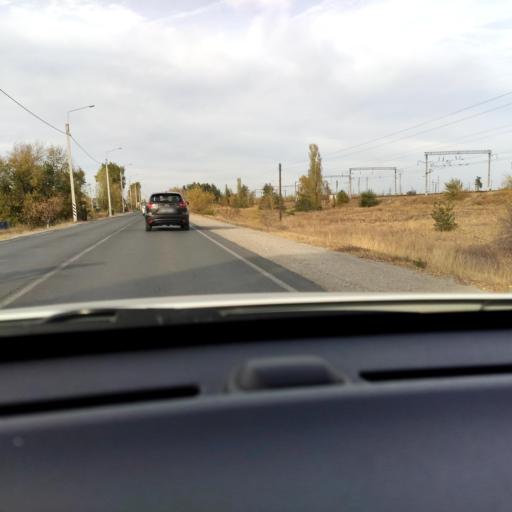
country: RU
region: Voronezj
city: Maslovka
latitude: 51.5727
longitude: 39.2465
